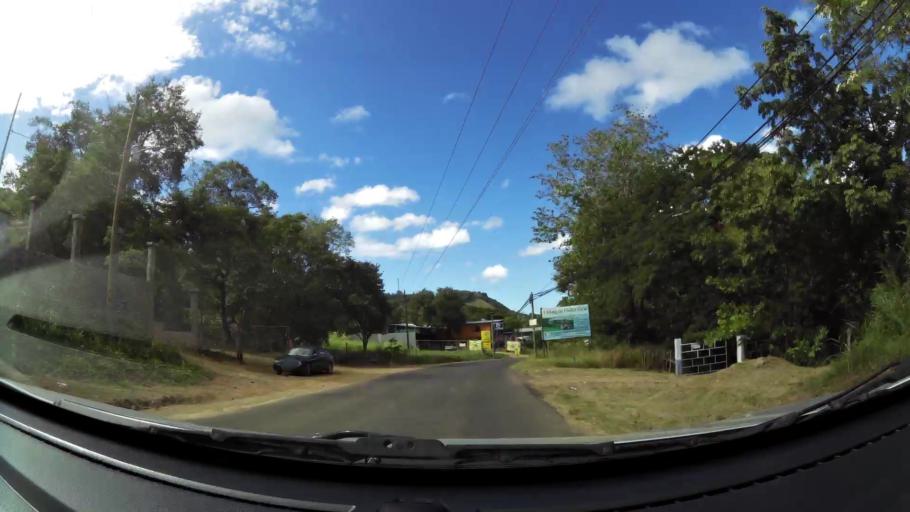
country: CR
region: Guanacaste
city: Santa Cruz
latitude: 10.3102
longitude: -85.8211
